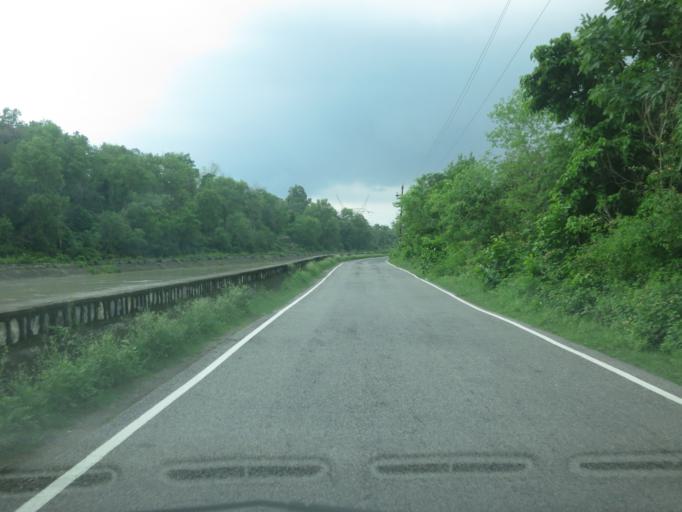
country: IN
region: Uttarakhand
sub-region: Dehradun
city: Raiwala
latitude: 29.9811
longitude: 78.2332
